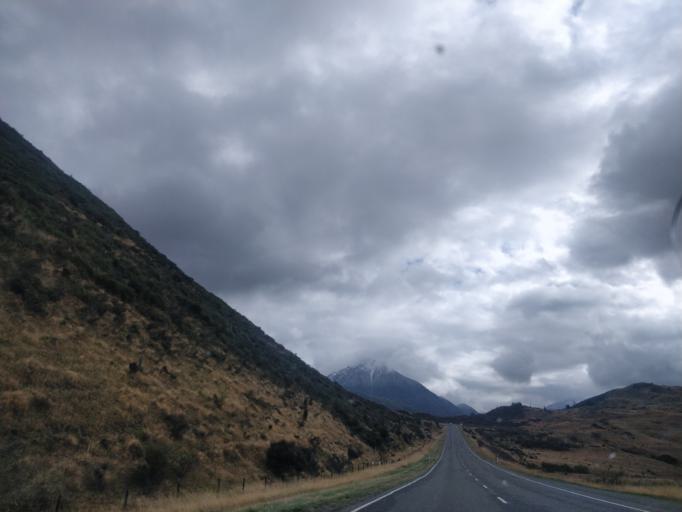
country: NZ
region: Canterbury
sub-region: Waimakariri District
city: Oxford
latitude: -43.0212
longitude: 171.7474
